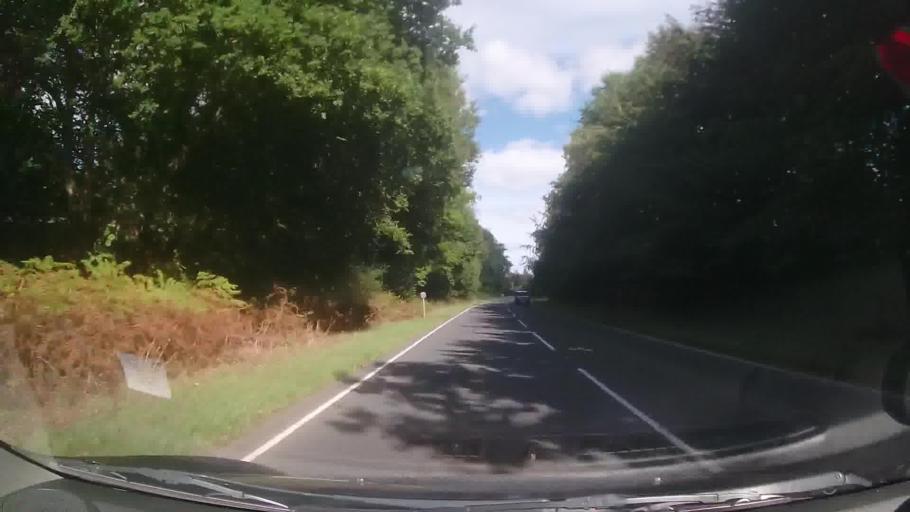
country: GB
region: England
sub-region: Herefordshire
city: Clifford
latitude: 52.1130
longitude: -3.1133
